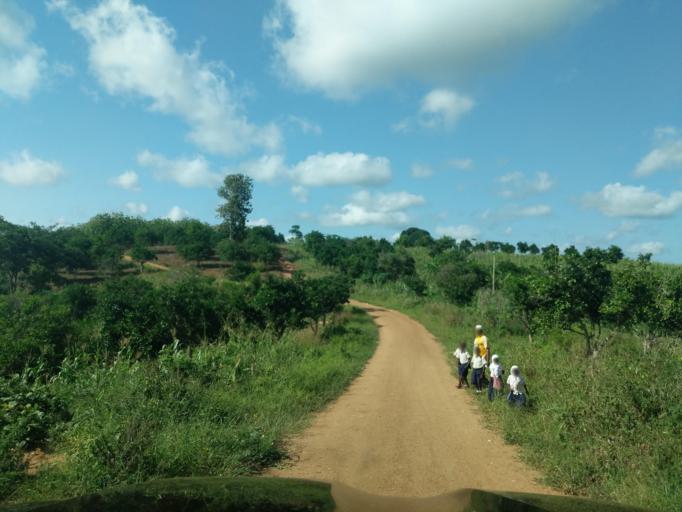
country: TZ
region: Tanga
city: Muheza
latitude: -5.4227
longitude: 38.6361
